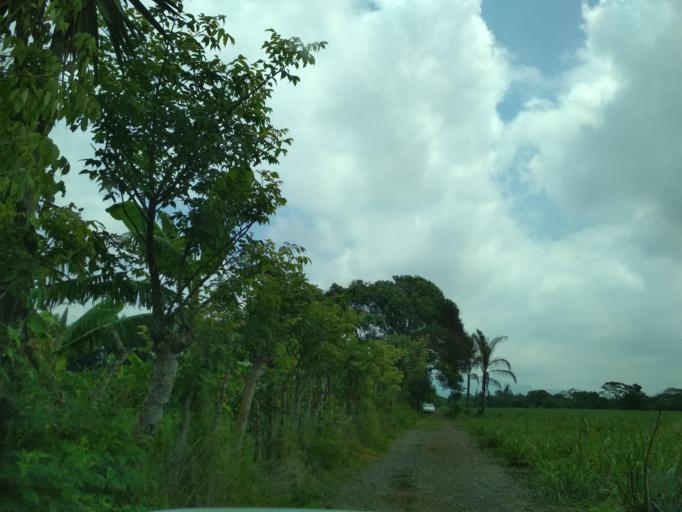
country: MX
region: Veracruz
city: Ixtac Zoquitlan
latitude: 18.8786
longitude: -97.0764
